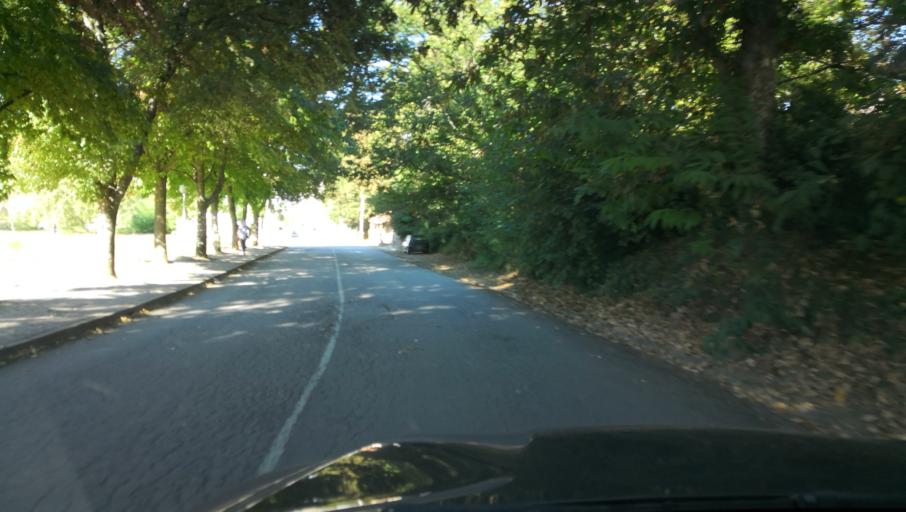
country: PT
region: Vila Real
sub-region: Vila Real
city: Vila Real
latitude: 41.2890
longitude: -7.7378
